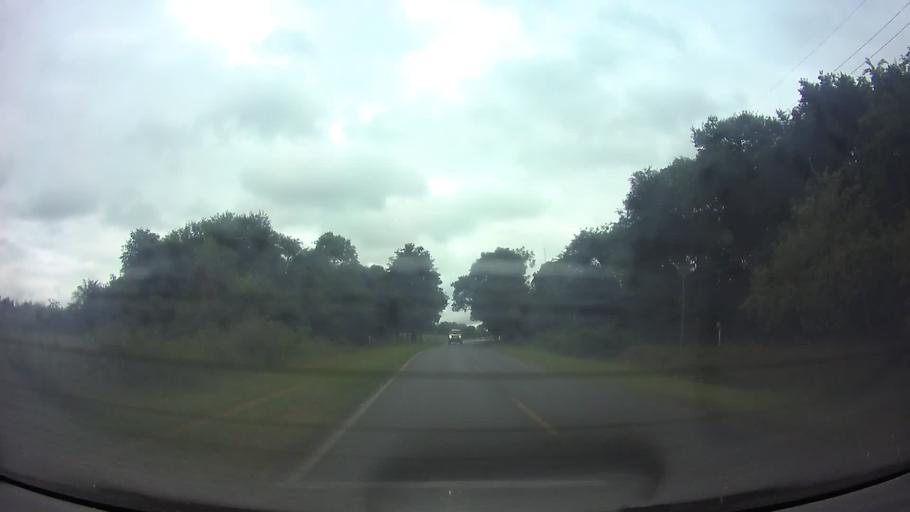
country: PY
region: Central
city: Guarambare
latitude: -25.5403
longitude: -57.5004
